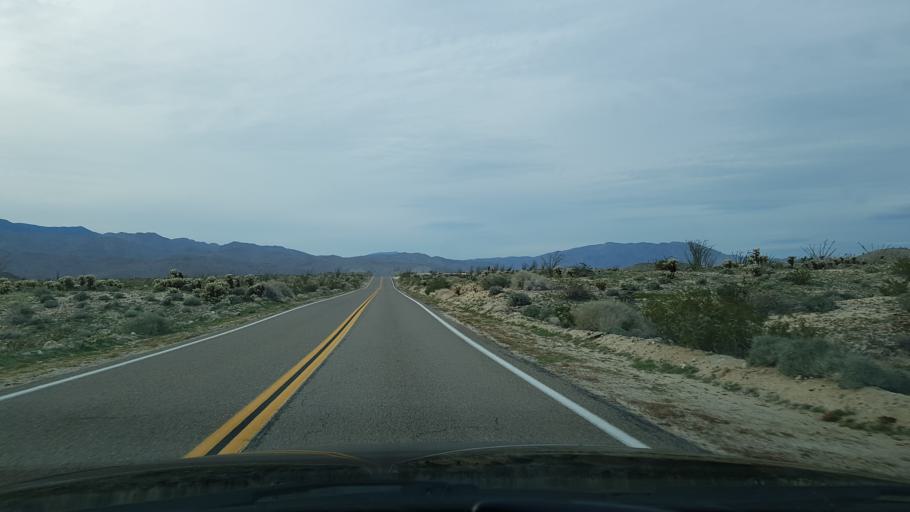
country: MX
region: Baja California
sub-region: Tecate
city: Cereso del Hongo
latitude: 32.8251
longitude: -116.1633
